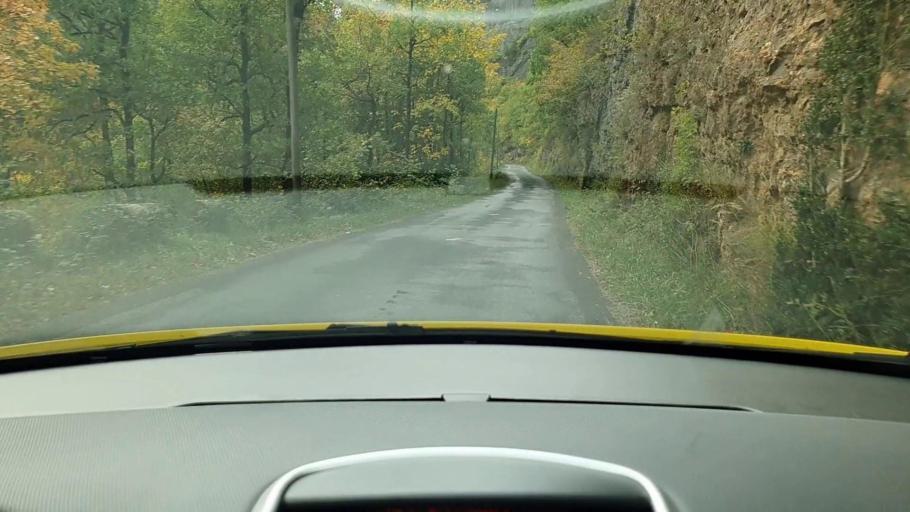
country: FR
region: Languedoc-Roussillon
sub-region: Departement de la Lozere
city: Meyrueis
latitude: 44.0947
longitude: 3.4037
